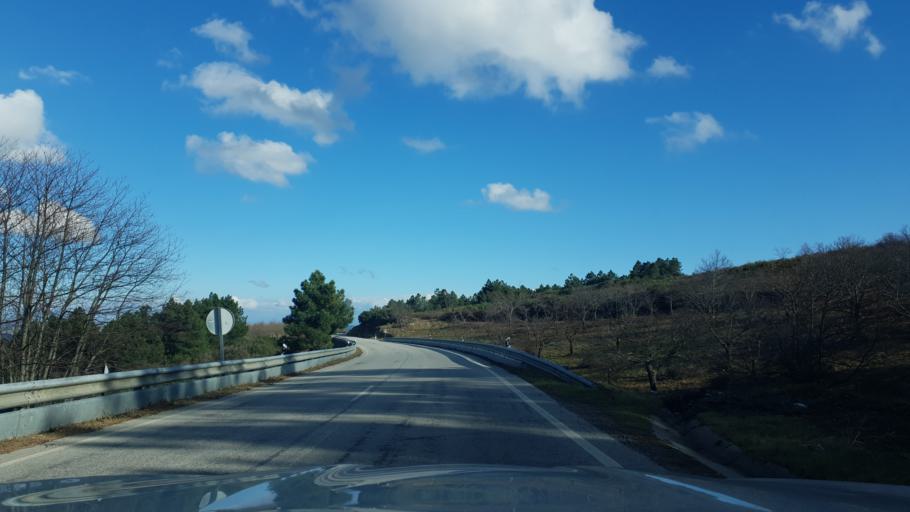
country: PT
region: Braganca
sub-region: Torre de Moncorvo
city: Torre de Moncorvo
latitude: 41.1854
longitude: -6.9482
